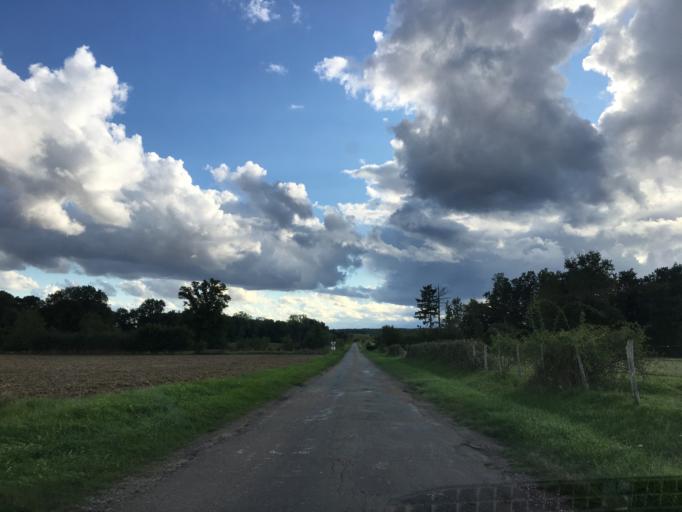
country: FR
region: Bourgogne
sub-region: Departement de l'Yonne
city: Saint-Georges-sur-Baulche
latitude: 47.8343
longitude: 3.5390
